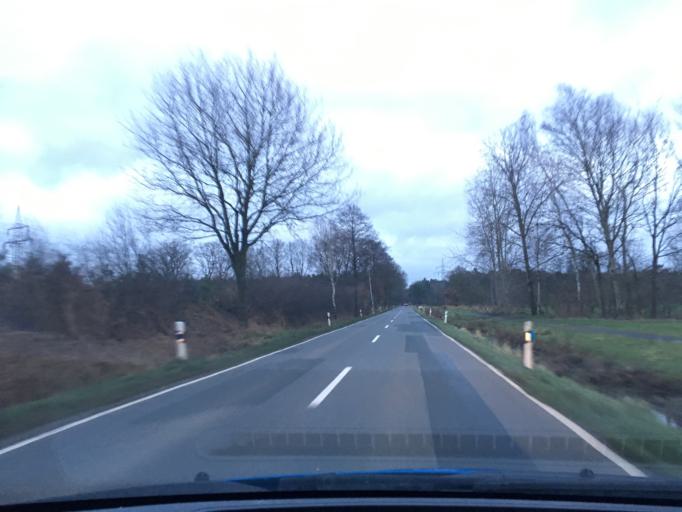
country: DE
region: Lower Saxony
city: Winsen
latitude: 53.3209
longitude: 10.2360
